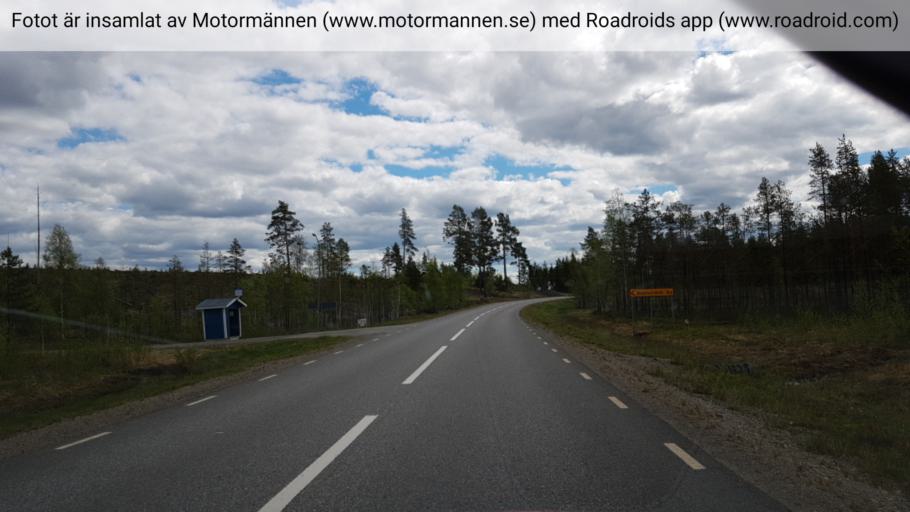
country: SE
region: Vaesterbotten
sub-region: Skelleftea Kommun
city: Langsele
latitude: 64.8169
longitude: 19.9858
